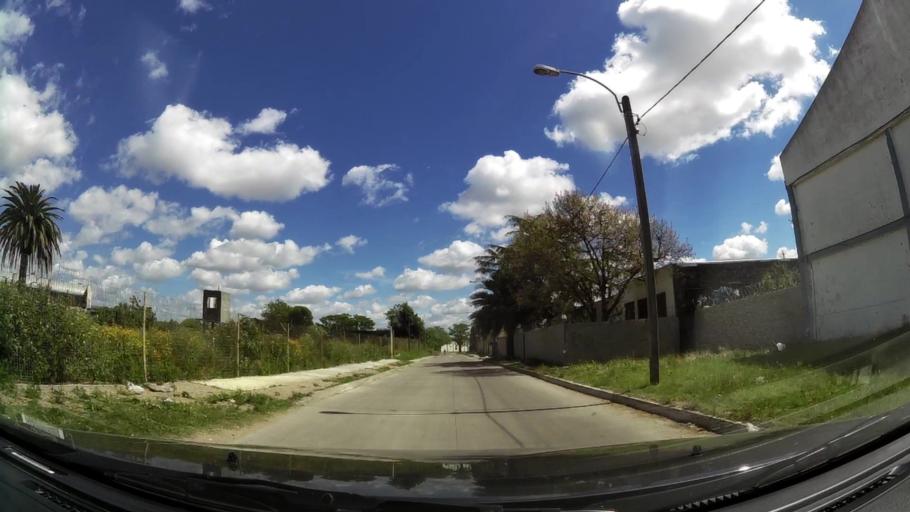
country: UY
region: Canelones
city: Paso de Carrasco
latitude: -34.8429
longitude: -56.1274
